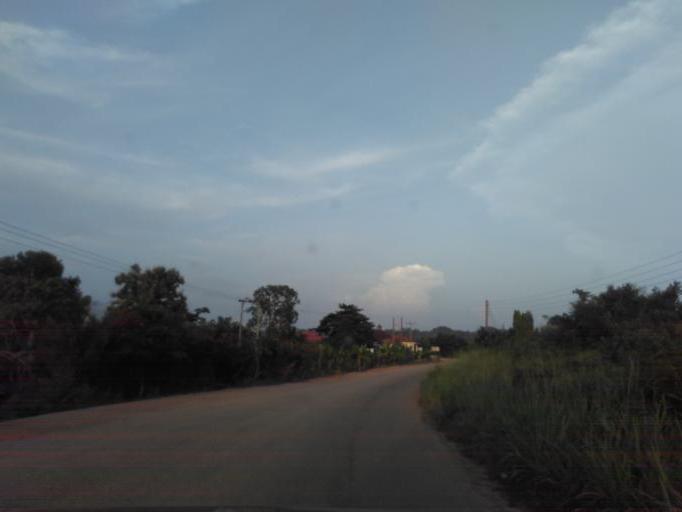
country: GH
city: Bekwai
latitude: 6.5411
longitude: -1.4690
